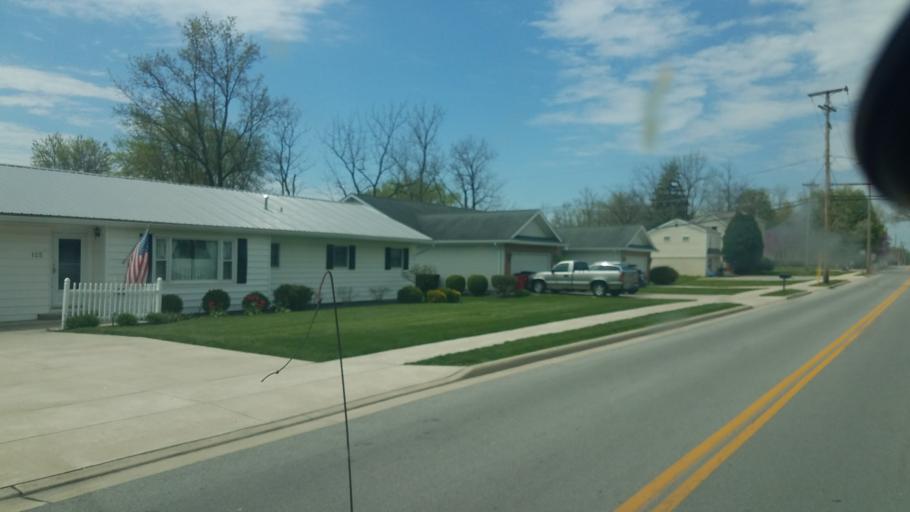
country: US
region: Ohio
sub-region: Hardin County
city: Ada
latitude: 40.7621
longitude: -83.8217
